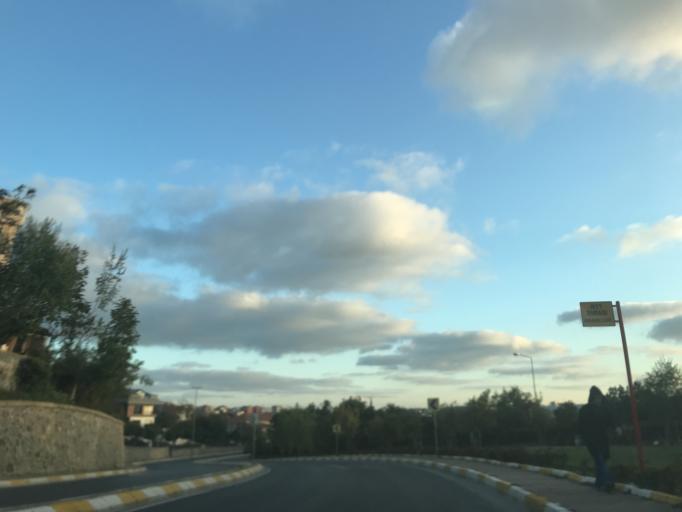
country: TR
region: Istanbul
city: Sisli
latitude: 41.1365
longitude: 29.0392
